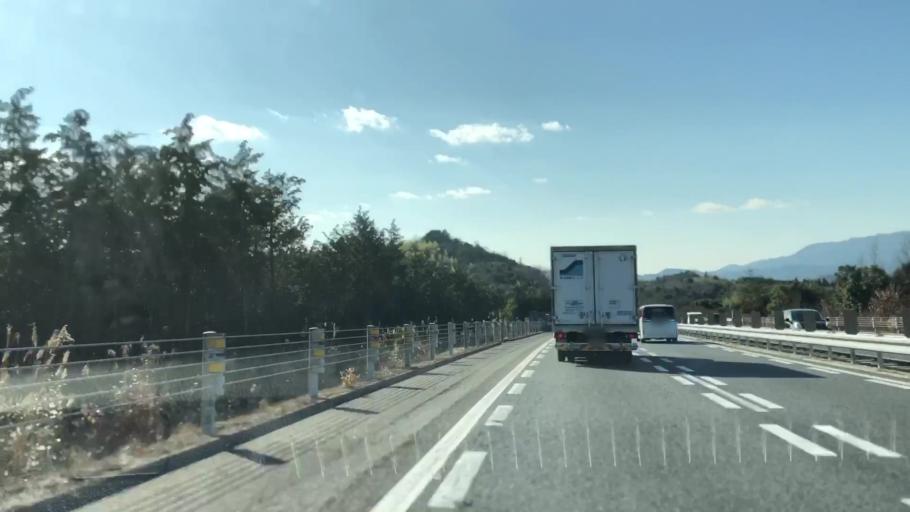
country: JP
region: Yamaguchi
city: Iwakuni
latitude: 34.1035
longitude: 132.1094
